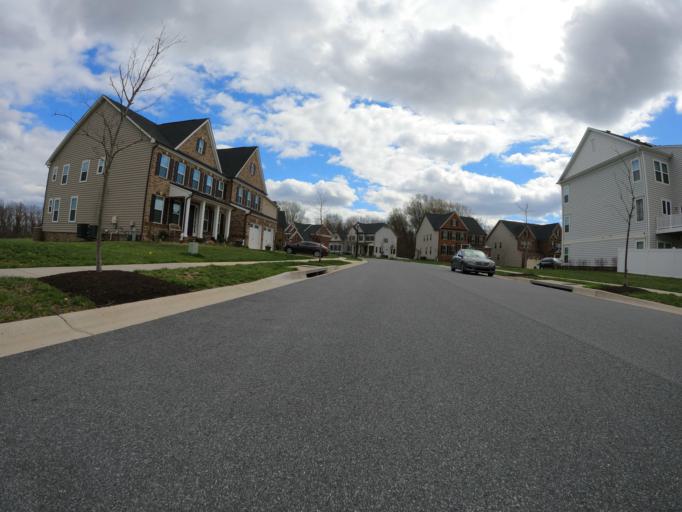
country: US
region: Maryland
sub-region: Howard County
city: North Laurel
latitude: 39.1465
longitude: -76.8500
